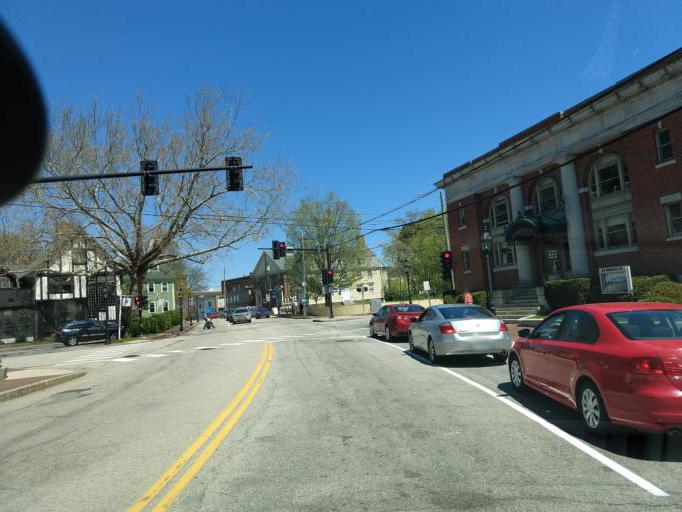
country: US
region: New Hampshire
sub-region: Rockingham County
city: Portsmouth
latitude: 43.0744
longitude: -70.7605
